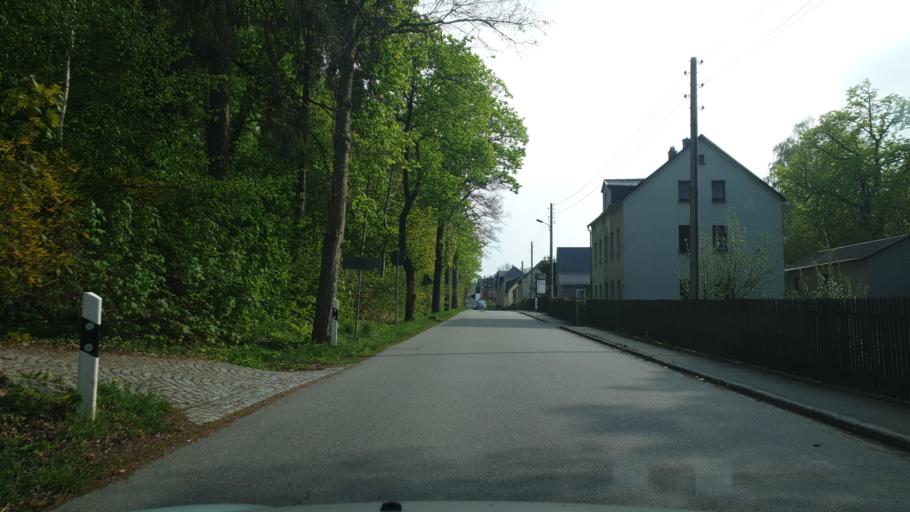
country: DE
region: Saxony
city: Stollberg
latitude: 50.7015
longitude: 12.7750
